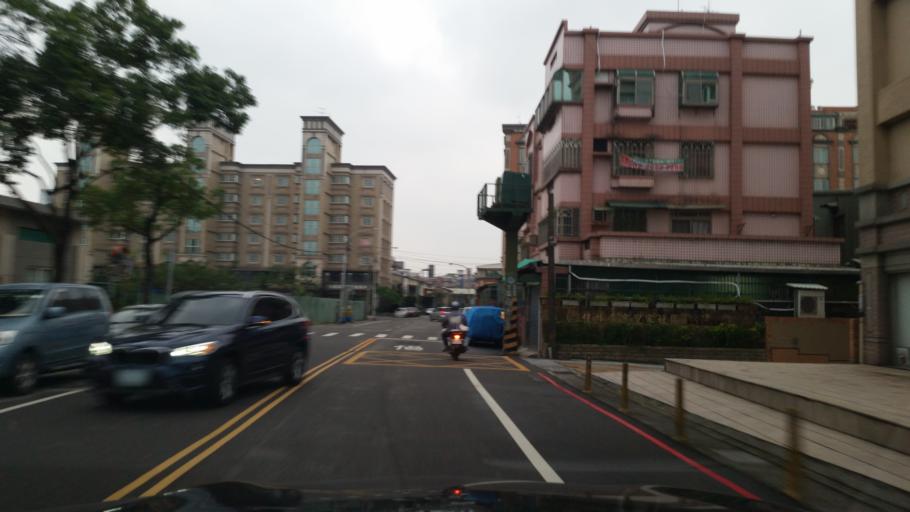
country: TW
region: Taiwan
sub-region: Taoyuan
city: Taoyuan
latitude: 25.0571
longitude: 121.3588
